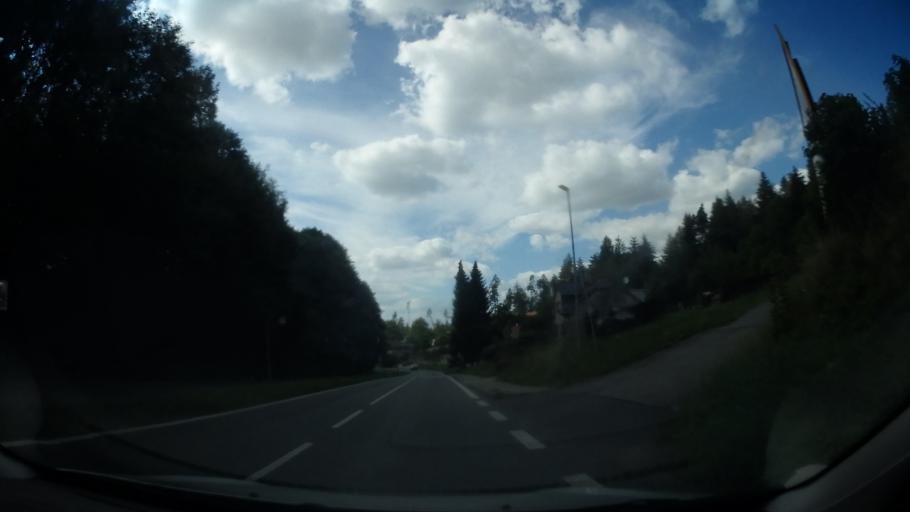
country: CZ
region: Vysocina
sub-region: Okres Zd'ar nad Sazavou
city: Nove Veseli
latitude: 49.5589
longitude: 15.8679
